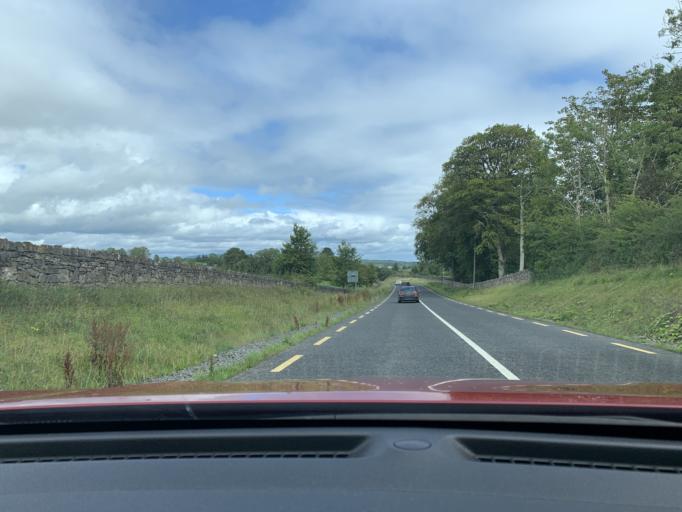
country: IE
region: Connaught
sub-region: County Leitrim
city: Carrick-on-Shannon
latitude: 53.9241
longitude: -8.1161
